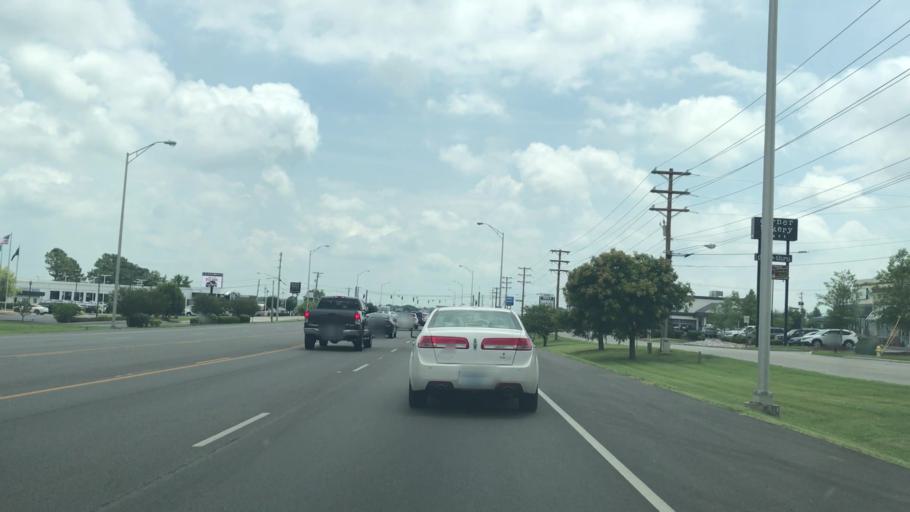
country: US
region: Kentucky
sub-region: Warren County
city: Bowling Green
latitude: 36.9619
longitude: -86.4306
